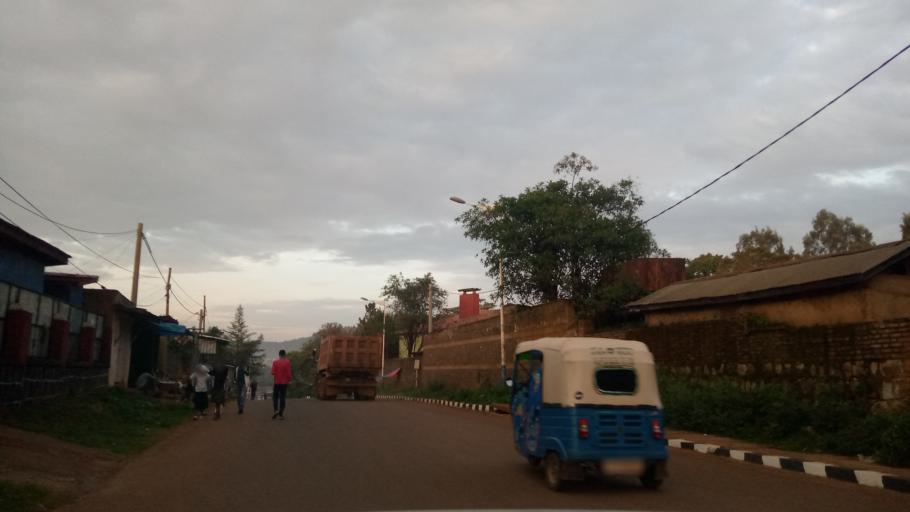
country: ET
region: Oromiya
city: Jima
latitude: 7.6751
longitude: 36.8269
